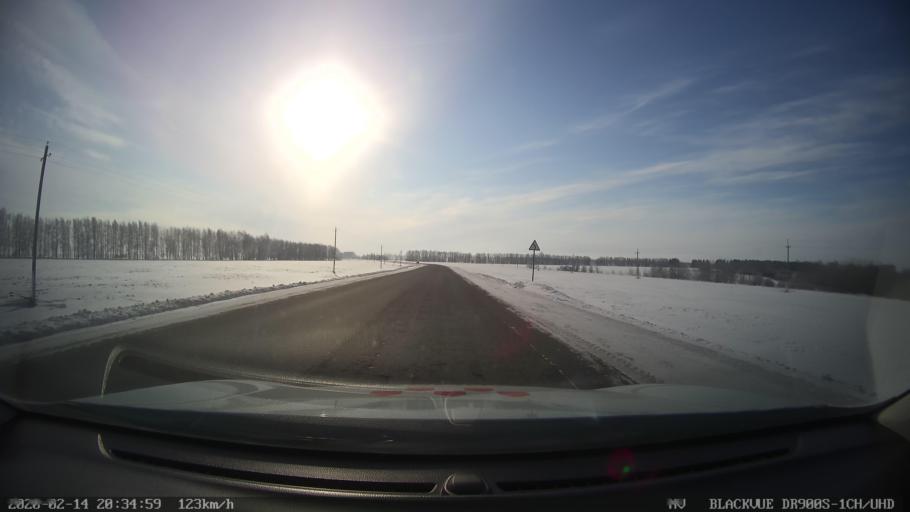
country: RU
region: Tatarstan
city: Kuybyshevskiy Zaton
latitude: 55.3895
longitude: 48.9796
